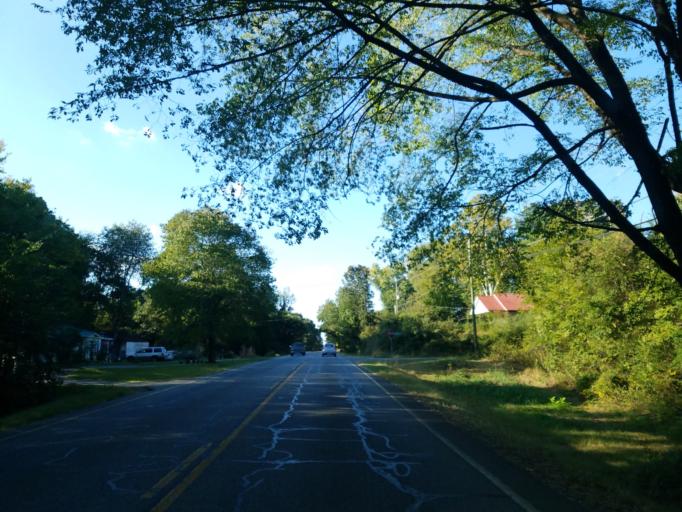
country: US
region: Georgia
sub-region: Bartow County
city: Cartersville
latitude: 34.1025
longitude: -84.8493
